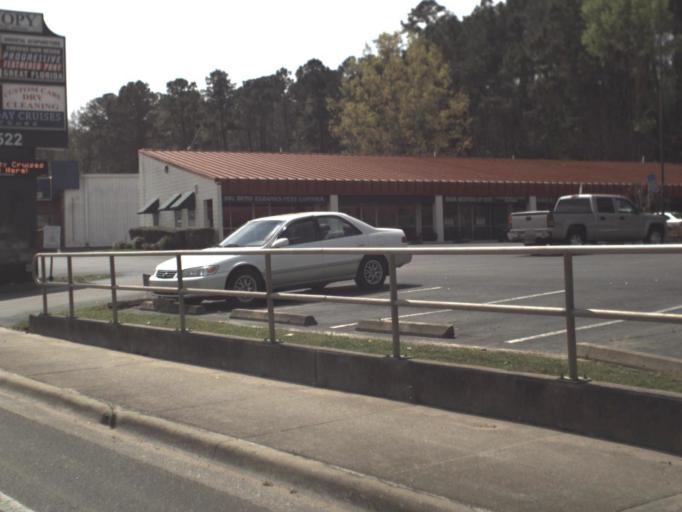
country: US
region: Florida
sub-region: Leon County
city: Tallahassee
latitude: 30.4855
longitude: -84.2375
